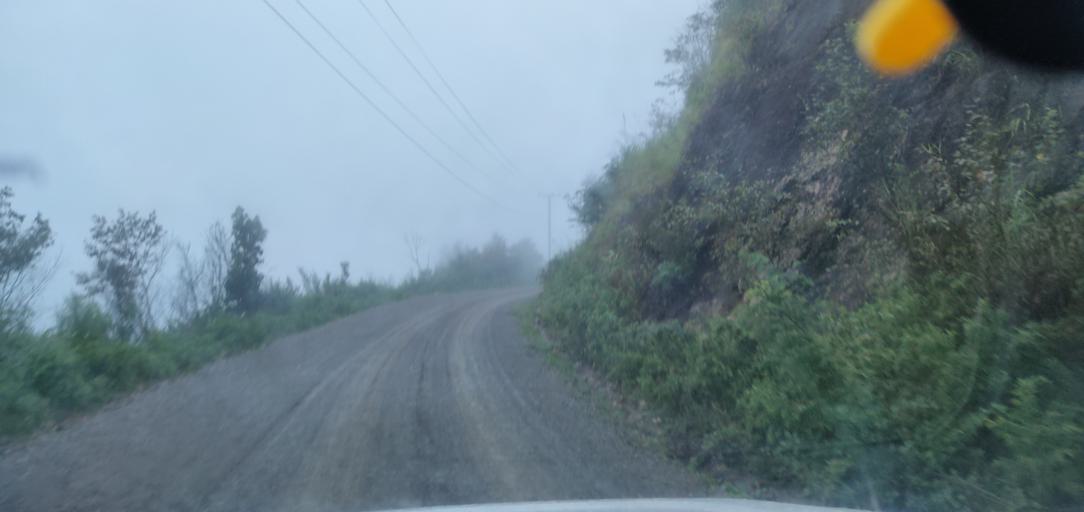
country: LA
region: Phongsali
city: Phongsali
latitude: 21.3949
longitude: 102.2061
